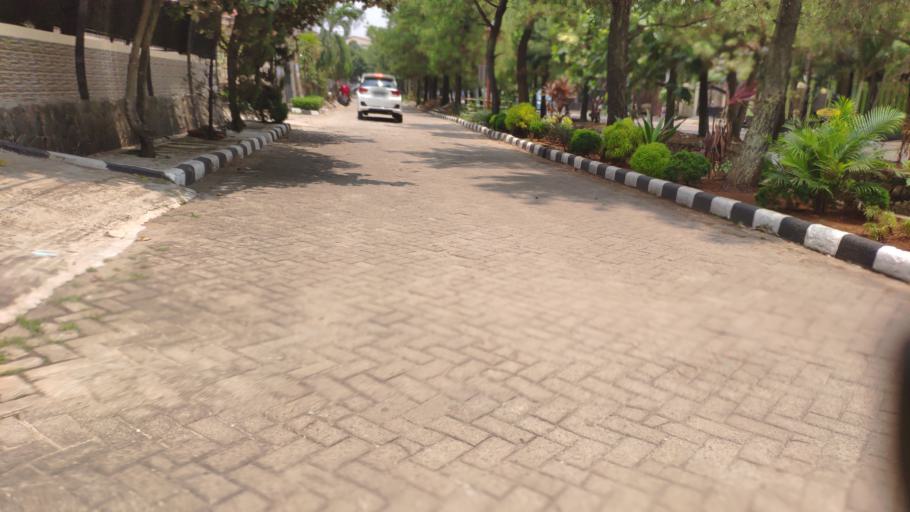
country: ID
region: West Java
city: Sawangan
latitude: -6.3977
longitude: 106.7936
